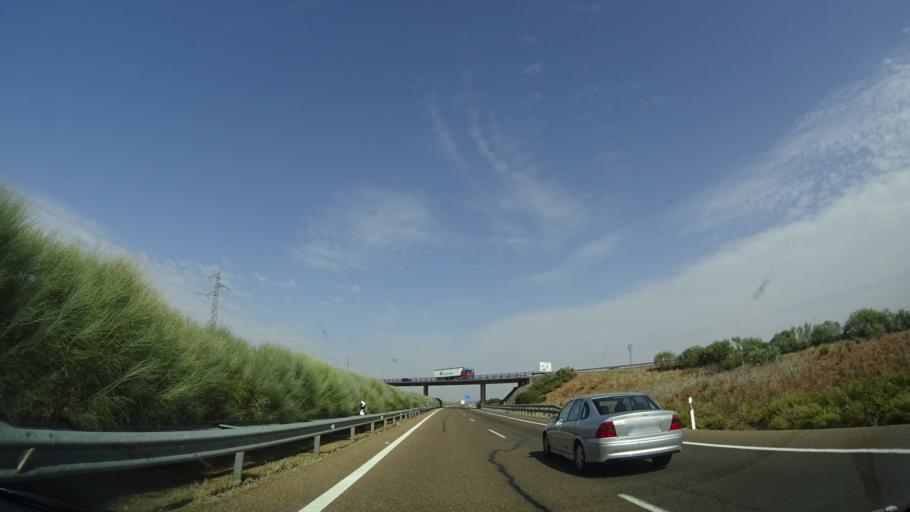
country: ES
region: Extremadura
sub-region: Provincia de Badajoz
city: Almendralejo
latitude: 38.6615
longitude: -6.3796
